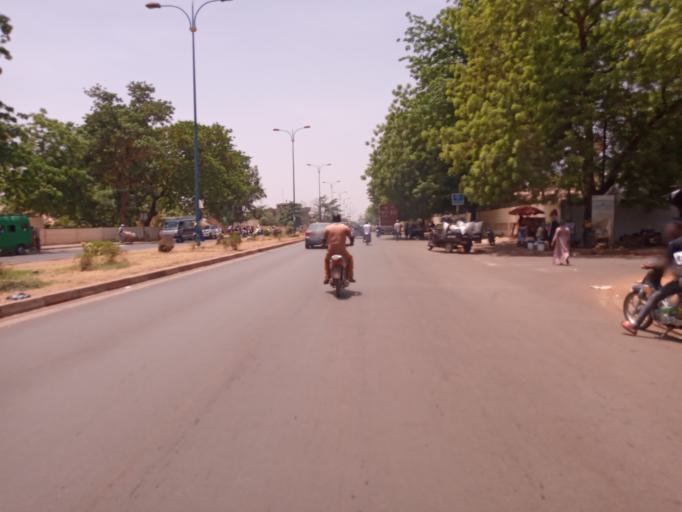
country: ML
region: Bamako
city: Bamako
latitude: 12.6361
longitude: -8.0059
